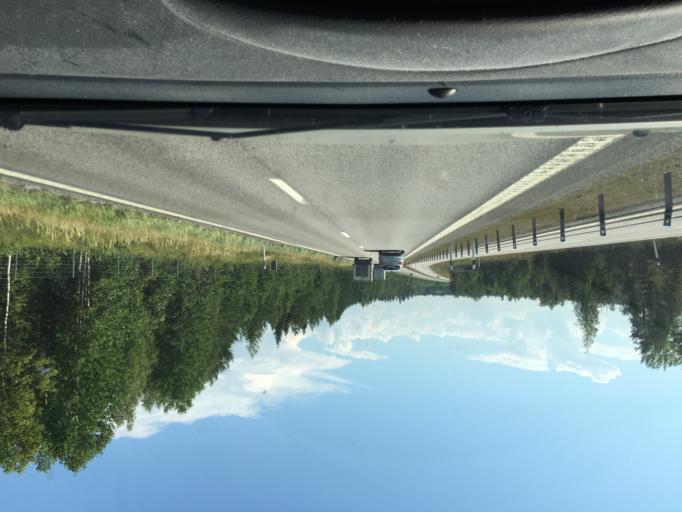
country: SE
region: Norrbotten
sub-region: Lulea Kommun
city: Gammelstad
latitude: 65.5825
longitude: 21.9731
